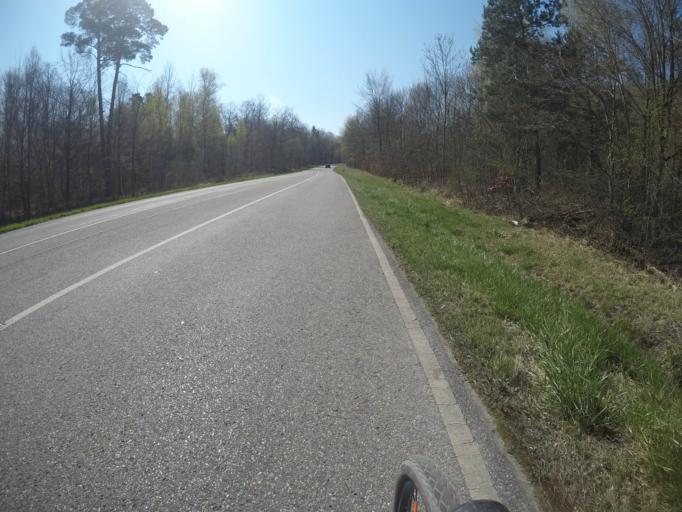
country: DE
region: Baden-Wuerttemberg
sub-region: Regierungsbezirk Stuttgart
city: Leonberg
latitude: 48.7562
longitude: 9.0383
